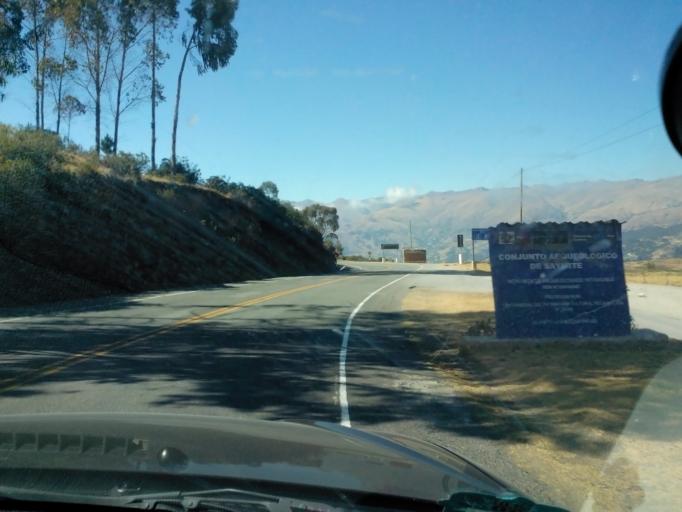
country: PE
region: Apurimac
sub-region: Provincia de Abancay
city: Cachora
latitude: -13.5405
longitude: -72.7987
